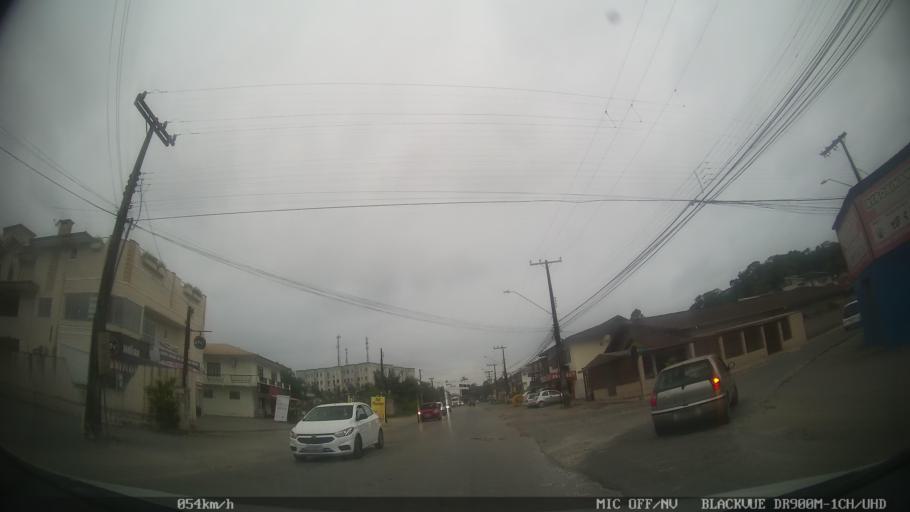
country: BR
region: Santa Catarina
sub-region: Joinville
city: Joinville
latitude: -26.3634
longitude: -48.8385
